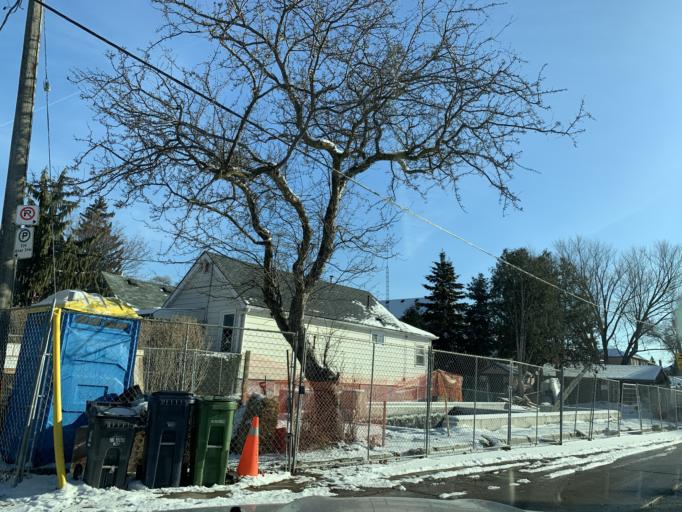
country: CA
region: Ontario
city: Toronto
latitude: 43.6820
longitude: -79.4861
